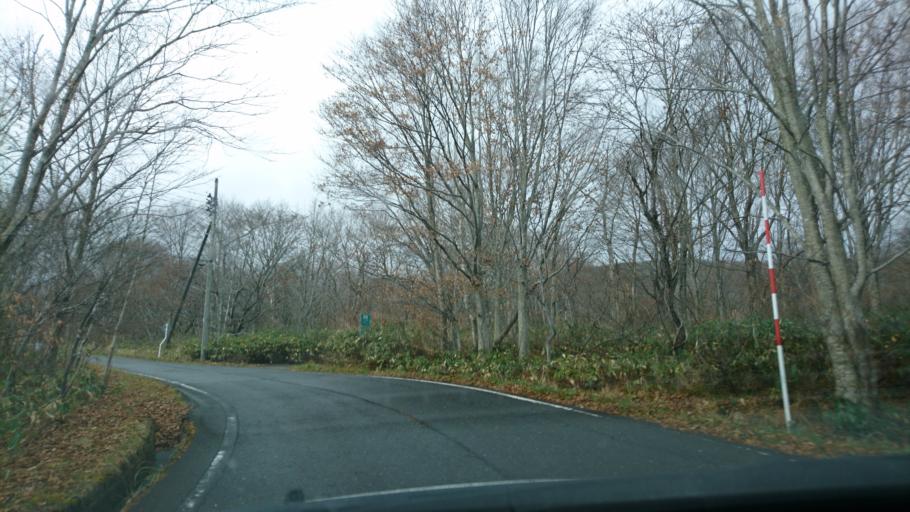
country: JP
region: Iwate
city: Ichinoseki
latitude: 38.9373
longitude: 140.8315
